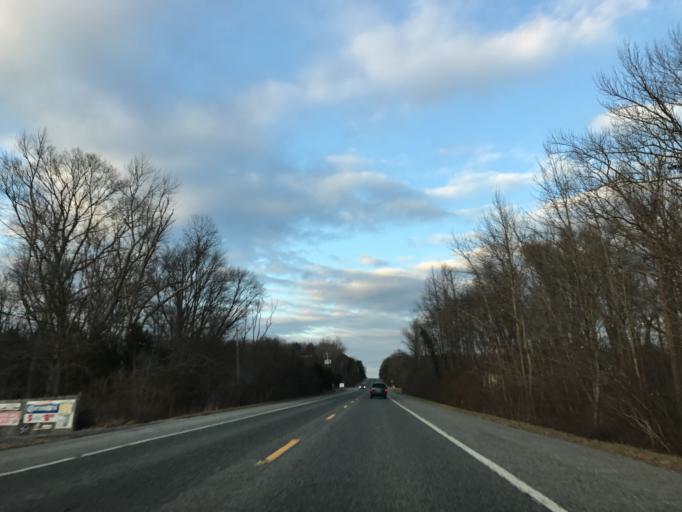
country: US
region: Maryland
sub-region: Cecil County
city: Charlestown
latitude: 39.5614
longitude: -75.9492
